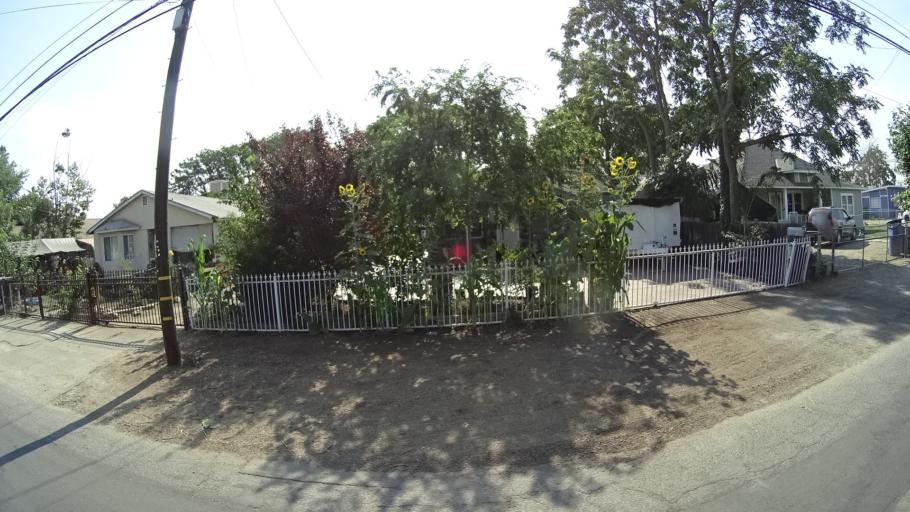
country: US
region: California
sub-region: Fresno County
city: Fresno
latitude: 36.7489
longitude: -119.8176
